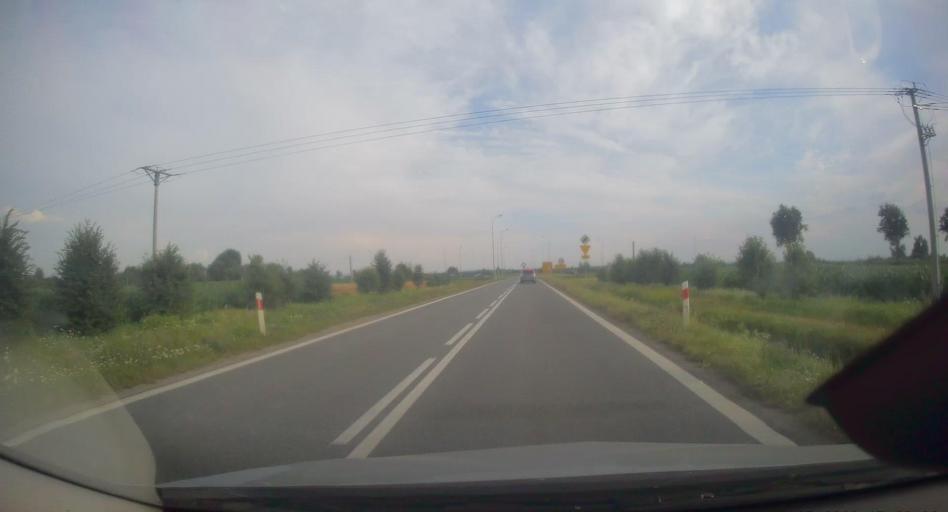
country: PL
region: Lesser Poland Voivodeship
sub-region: Powiat brzeski
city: Szczurowa
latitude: 50.1249
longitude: 20.6127
